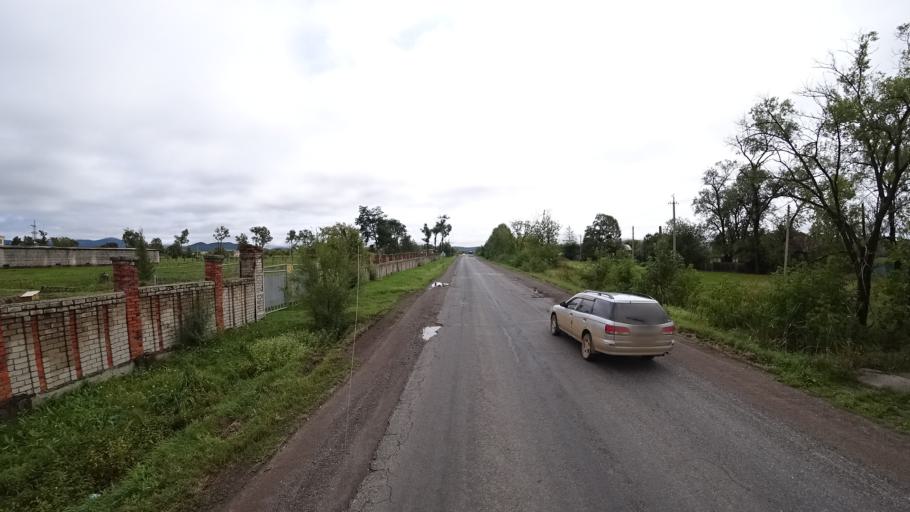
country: RU
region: Primorskiy
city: Monastyrishche
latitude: 44.2037
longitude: 132.4744
